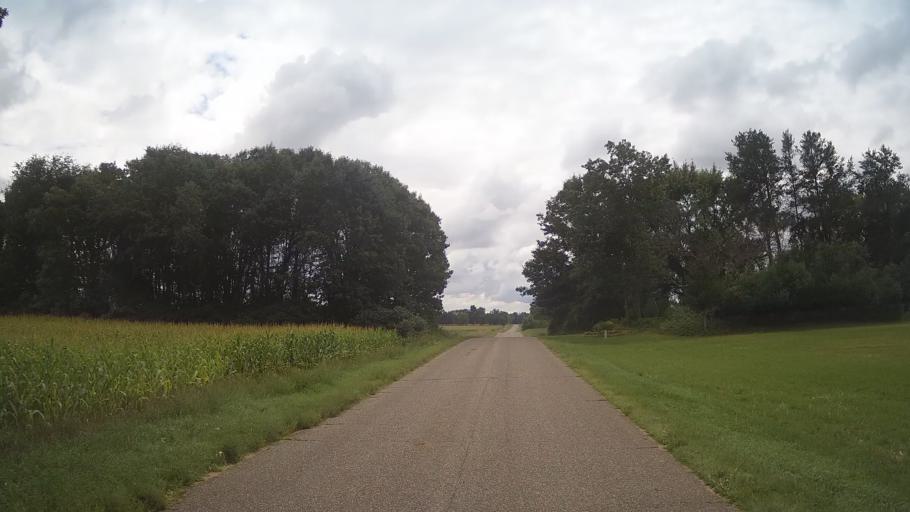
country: US
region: Wisconsin
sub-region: Adams County
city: Friendship
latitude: 44.0357
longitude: -89.9177
